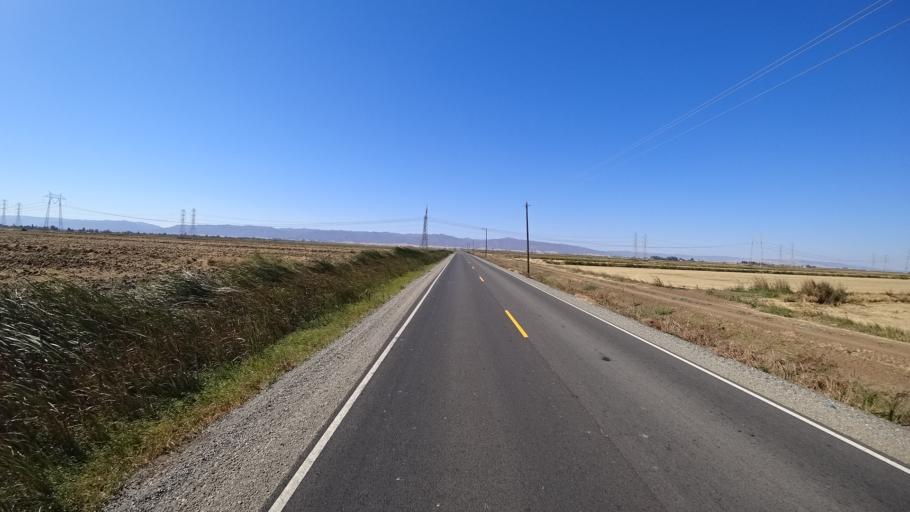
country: US
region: California
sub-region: Yolo County
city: Cottonwood
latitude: 38.6202
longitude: -121.9302
